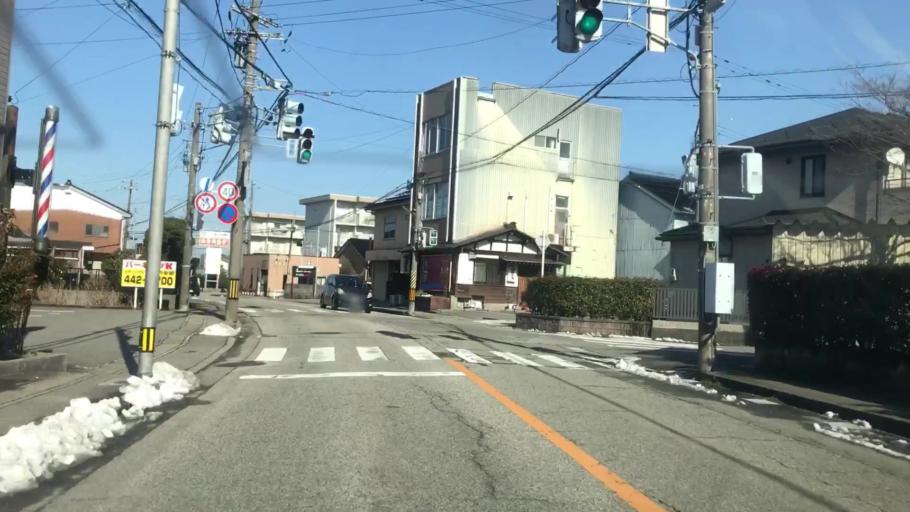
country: JP
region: Toyama
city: Toyama-shi
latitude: 36.6731
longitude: 137.2406
